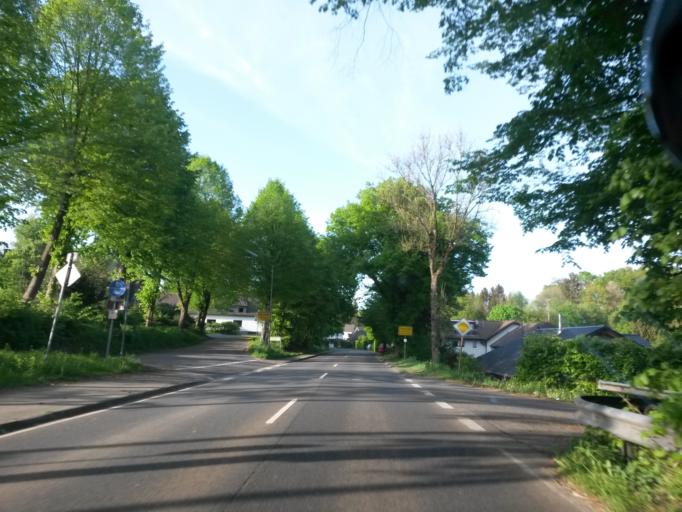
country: DE
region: North Rhine-Westphalia
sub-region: Regierungsbezirk Koln
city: Much
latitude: 50.9256
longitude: 7.4388
